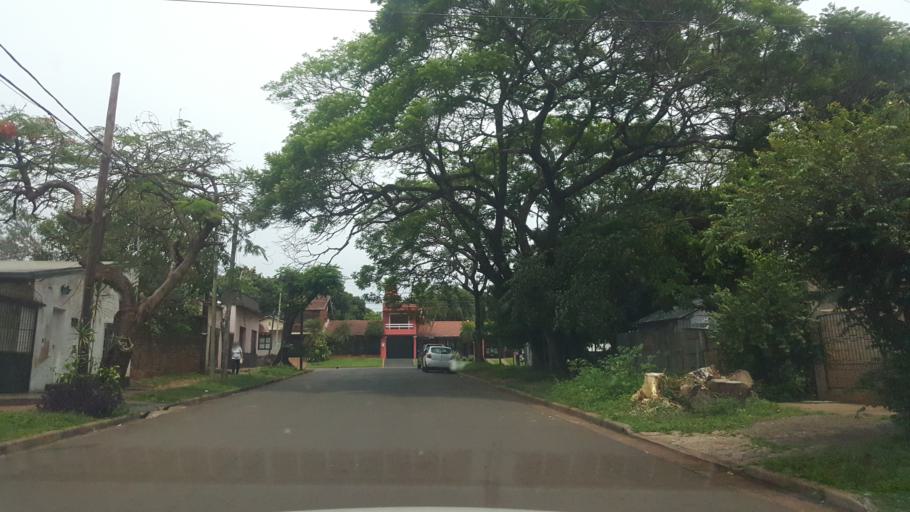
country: AR
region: Misiones
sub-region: Departamento de Capital
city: Posadas
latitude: -27.3684
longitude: -55.9148
